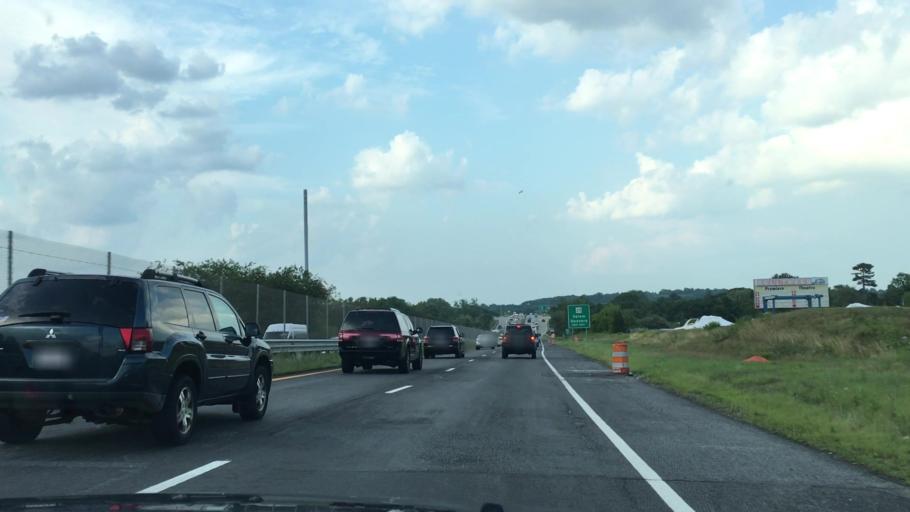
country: US
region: Massachusetts
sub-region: Essex County
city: Danvers
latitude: 42.5530
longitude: -70.9348
